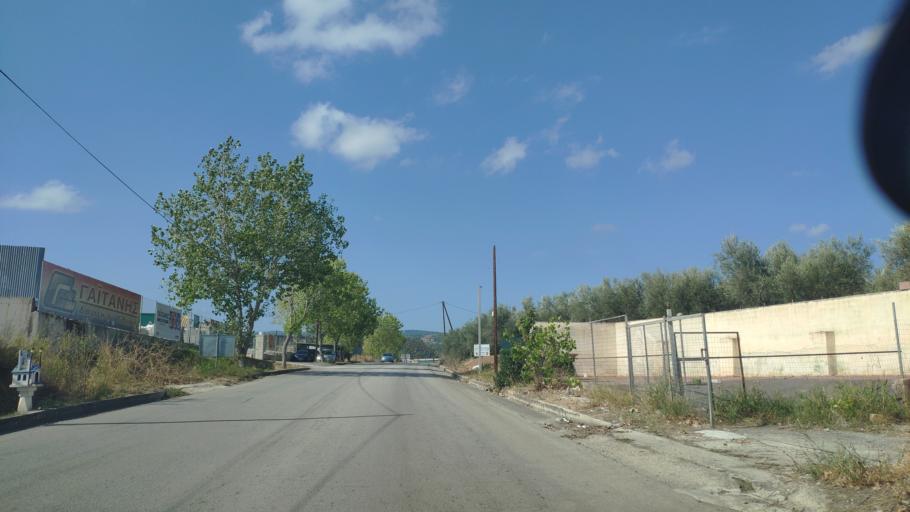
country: GR
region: Peloponnese
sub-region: Nomos Korinthias
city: Pasion
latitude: 38.0053
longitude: 22.7302
